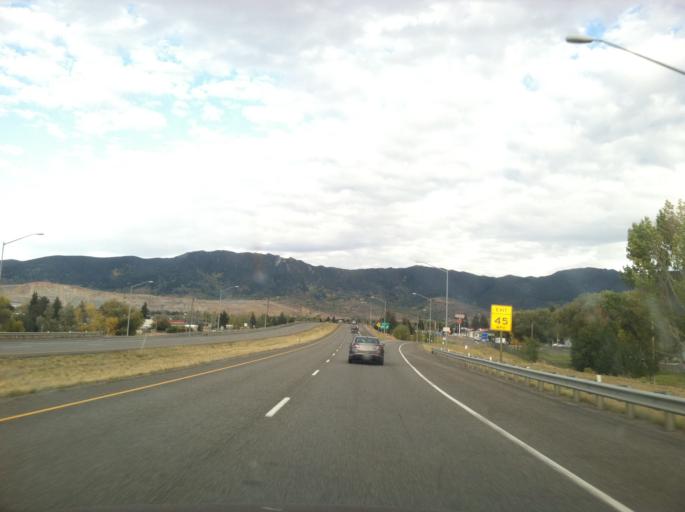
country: US
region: Montana
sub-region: Silver Bow County
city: Butte
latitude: 45.9924
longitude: -112.5447
